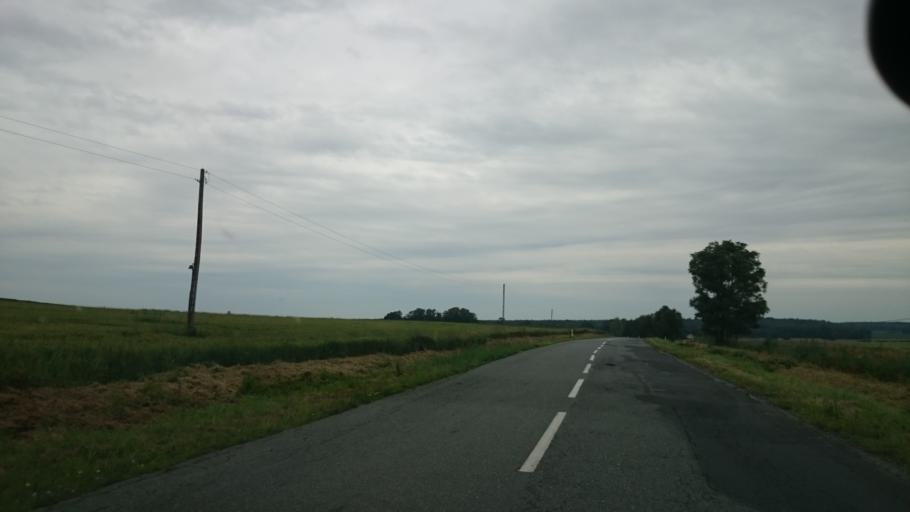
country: PL
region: Lower Silesian Voivodeship
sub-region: Powiat strzelinski
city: Przeworno
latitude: 50.6441
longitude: 17.2158
